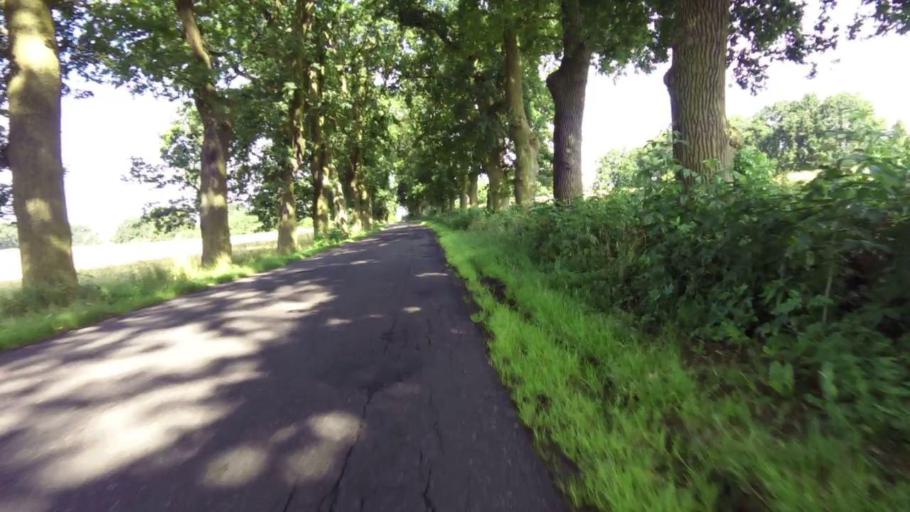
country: PL
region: West Pomeranian Voivodeship
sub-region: Powiat stargardzki
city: Stara Dabrowa
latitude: 53.3431
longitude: 15.1639
